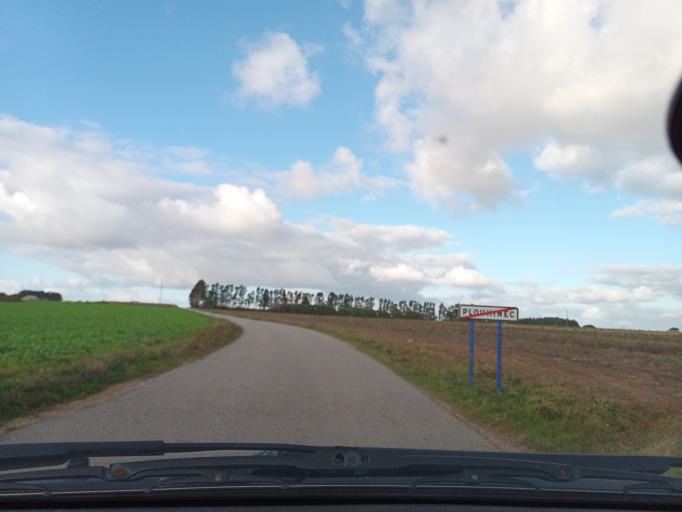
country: FR
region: Brittany
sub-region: Departement du Finistere
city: Plouhinec
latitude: 48.0190
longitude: -4.4990
